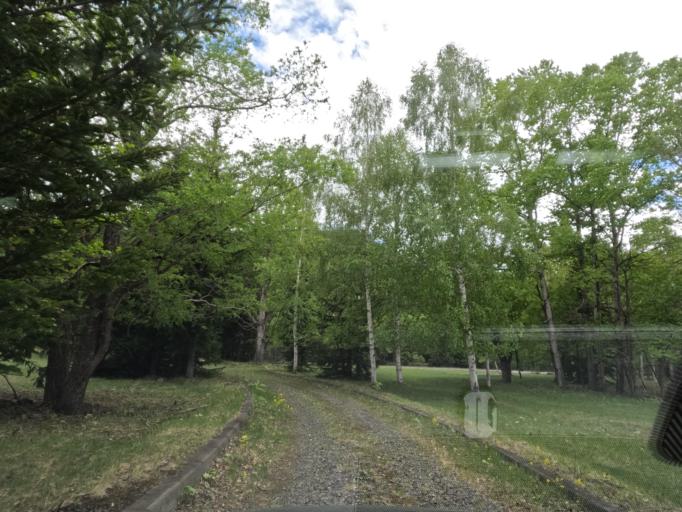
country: JP
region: Hokkaido
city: Kamikawa
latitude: 43.6429
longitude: 143.0226
